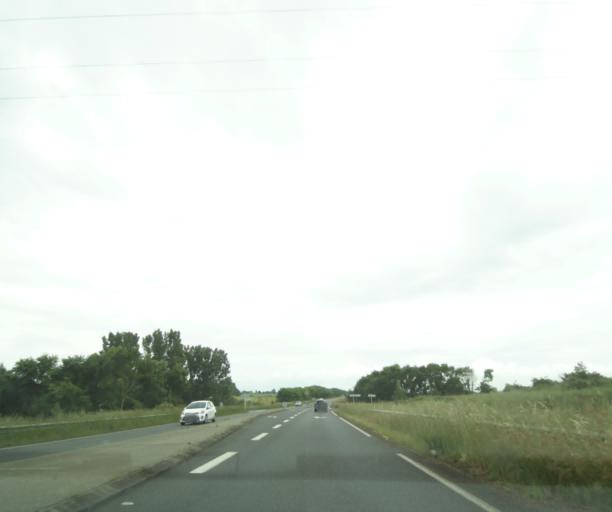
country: FR
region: Poitou-Charentes
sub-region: Departement des Deux-Sevres
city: Airvault
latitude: 46.8099
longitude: -0.2109
